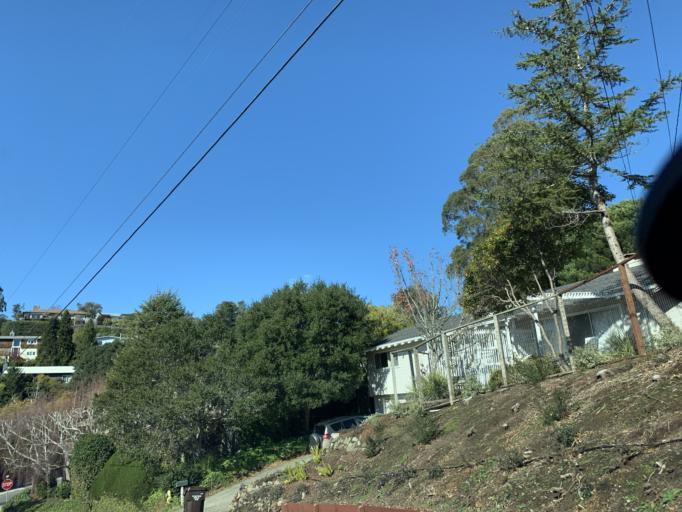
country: US
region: California
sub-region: Marin County
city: Strawberry
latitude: 37.9003
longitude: -122.5213
